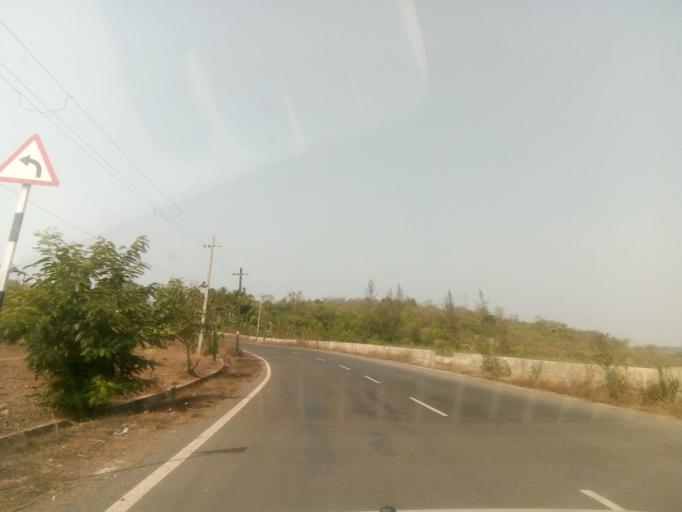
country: IN
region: Goa
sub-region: North Goa
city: Colovale
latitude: 15.6885
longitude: 73.8397
